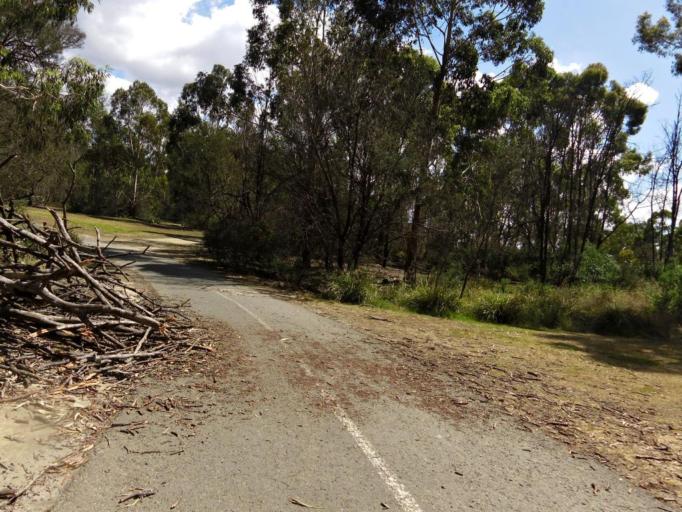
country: AU
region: Victoria
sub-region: Nillumbik
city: Eltham North
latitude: -37.6938
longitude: 145.1525
